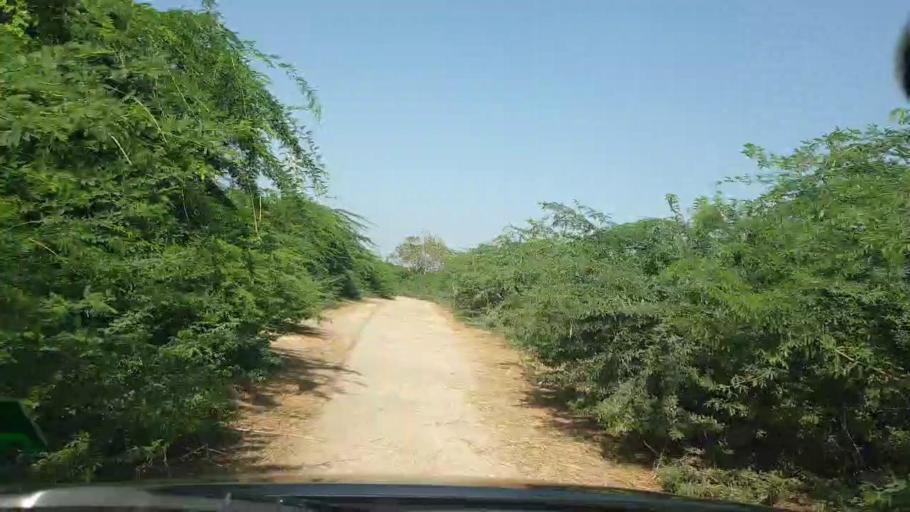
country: PK
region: Sindh
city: Tando Bago
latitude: 24.7716
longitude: 68.9557
